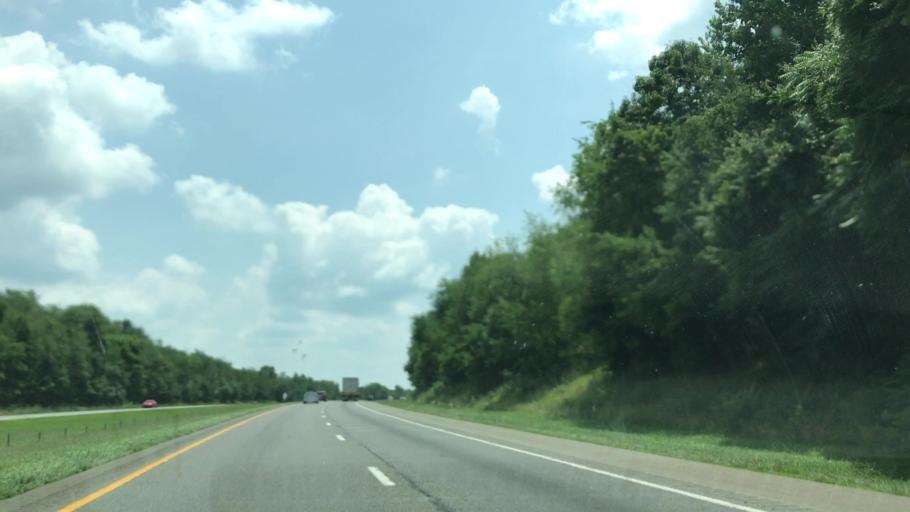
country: US
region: North Carolina
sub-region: Surry County
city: Dobson
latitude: 36.3312
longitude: -80.7941
